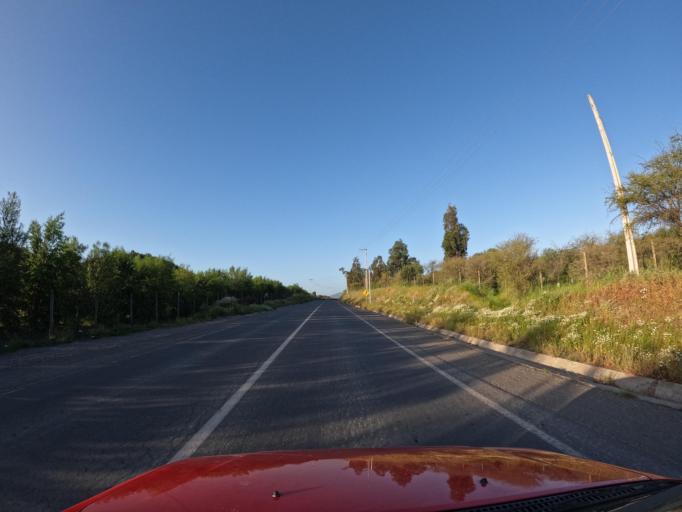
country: CL
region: O'Higgins
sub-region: Provincia de Colchagua
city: Santa Cruz
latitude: -34.3208
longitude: -71.3895
